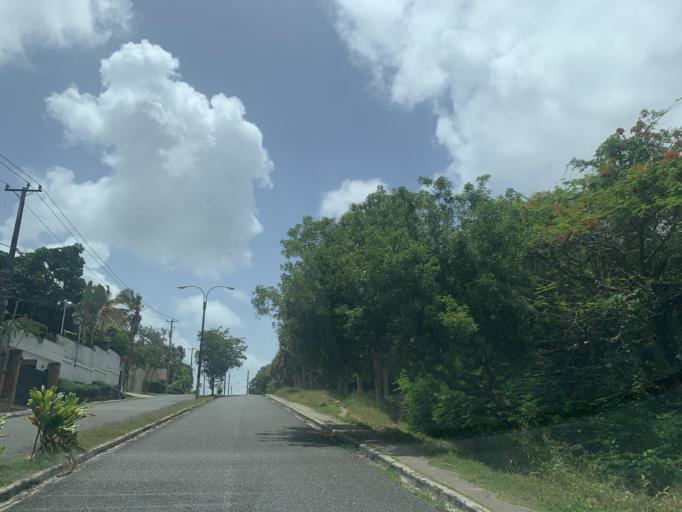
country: DO
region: Nacional
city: La Agustina
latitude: 18.5002
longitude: -69.9511
